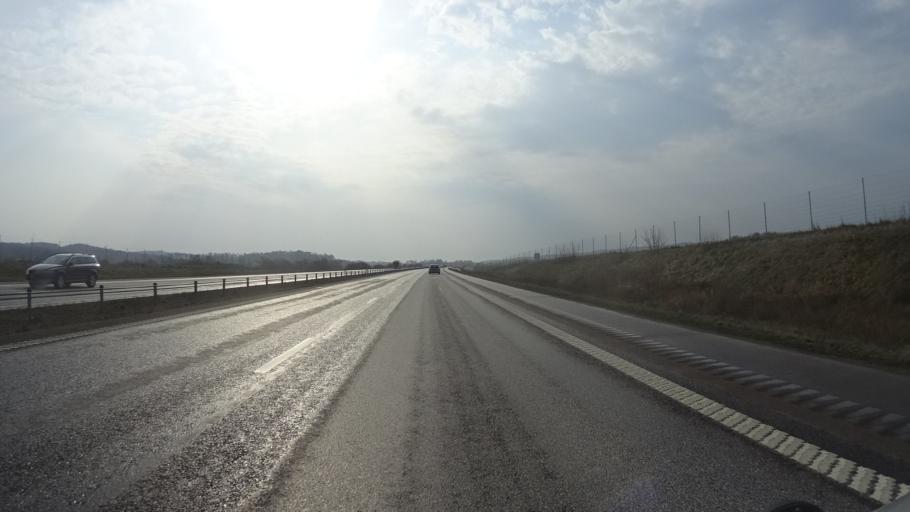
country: SE
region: Halland
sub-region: Halmstads Kommun
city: Getinge
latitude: 56.7936
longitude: 12.7843
